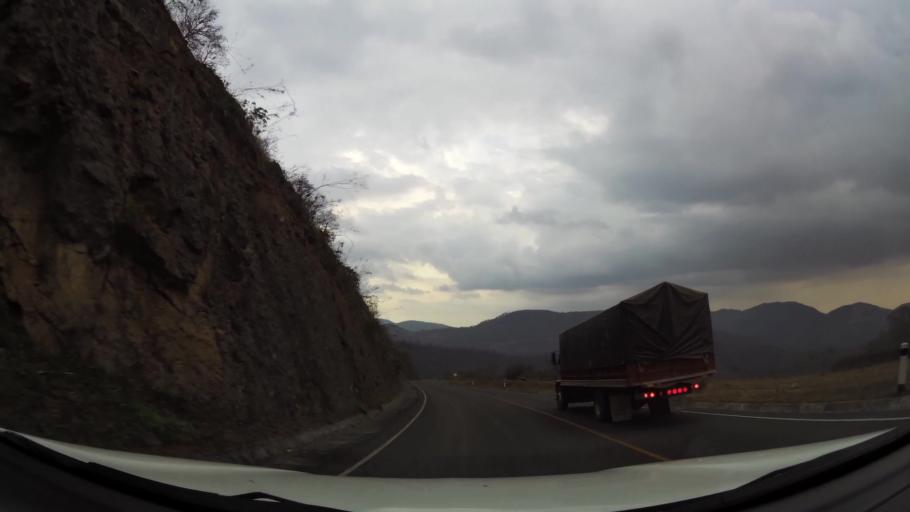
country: NI
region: Jinotega
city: Jinotega
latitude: 13.0433
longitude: -86.0035
